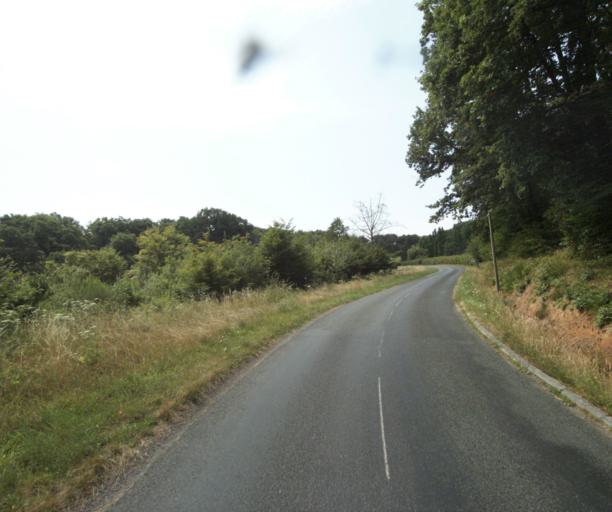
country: FR
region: Bourgogne
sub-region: Departement de Saone-et-Loire
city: Gueugnon
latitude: 46.5915
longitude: 4.0820
